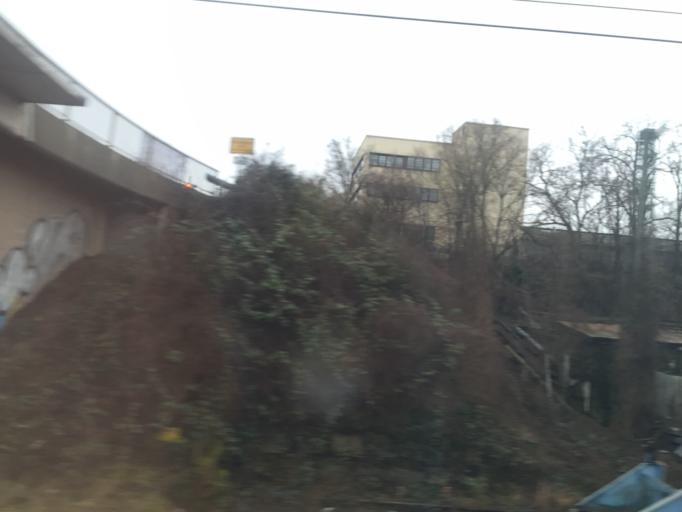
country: DE
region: Baden-Wuerttemberg
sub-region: Regierungsbezirk Stuttgart
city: Gemmrigheim
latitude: 49.0340
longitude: 9.1504
